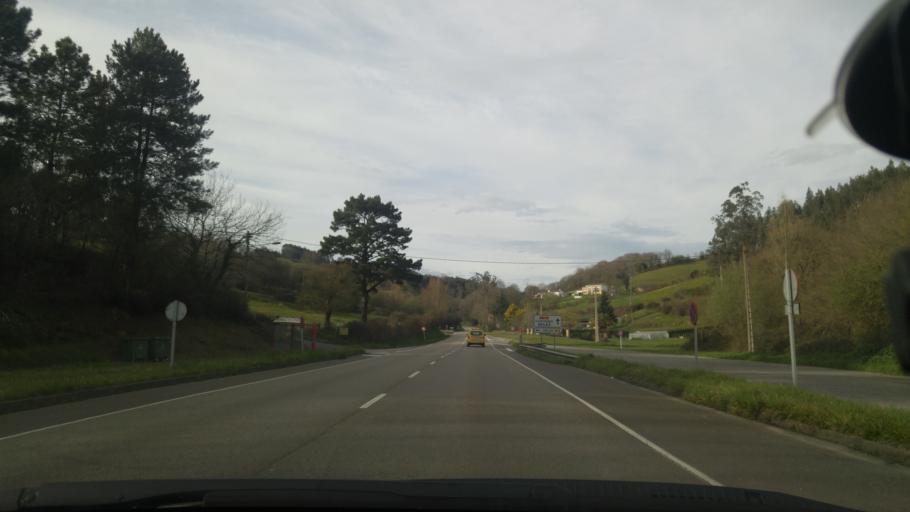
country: ES
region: Asturias
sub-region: Province of Asturias
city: Llanera
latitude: 43.4507
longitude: -5.8545
